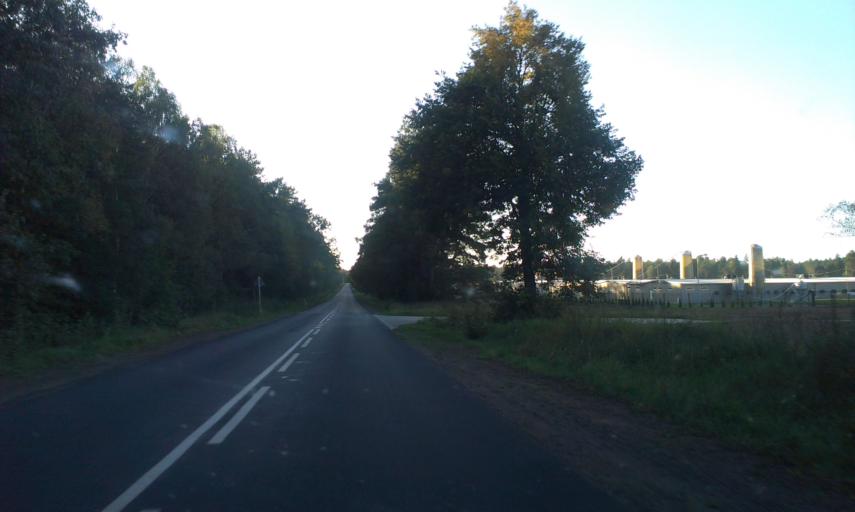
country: PL
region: Pomeranian Voivodeship
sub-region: Powiat czluchowski
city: Rzeczenica
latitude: 53.6548
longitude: 17.1383
